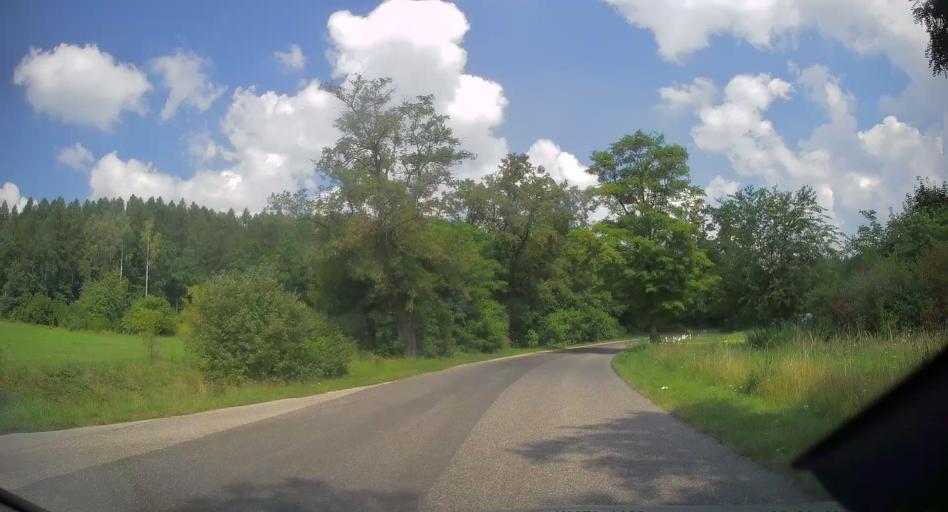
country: PL
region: Swietokrzyskie
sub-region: Powiat kielecki
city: Checiny
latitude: 50.7958
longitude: 20.4544
